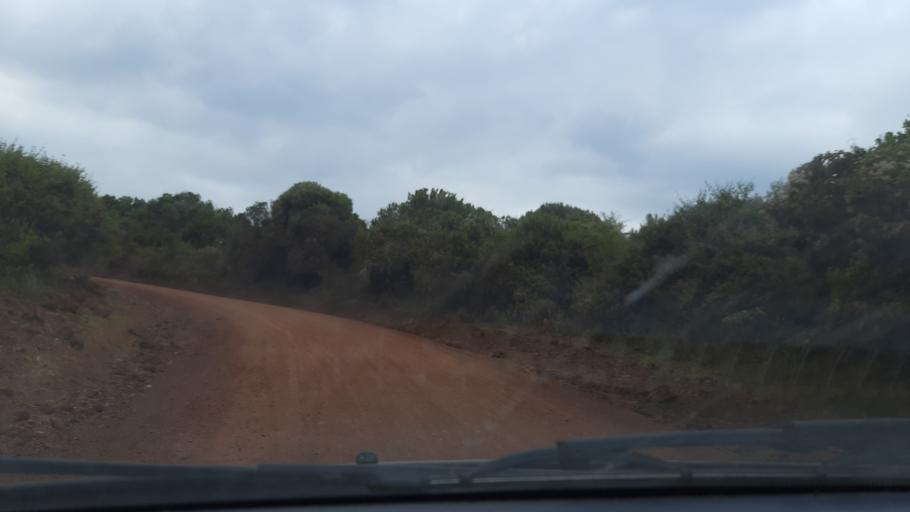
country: TZ
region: Kilimanjaro
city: Moshi
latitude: -2.8601
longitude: 37.2524
